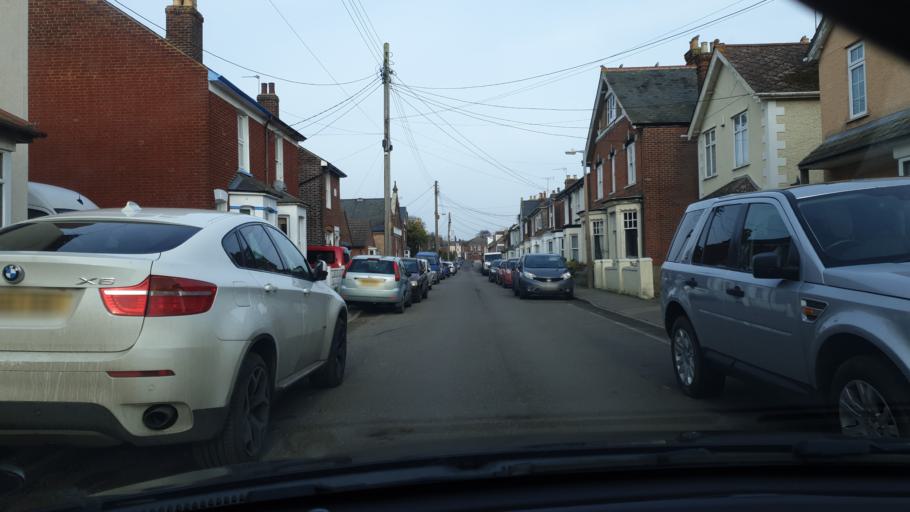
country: GB
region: England
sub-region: Essex
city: Brightlingsea
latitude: 51.8082
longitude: 1.0259
